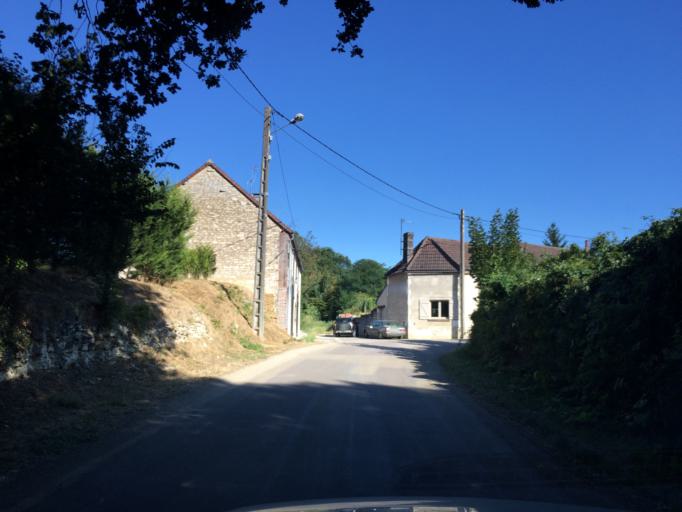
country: FR
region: Bourgogne
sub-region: Departement de l'Yonne
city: Fleury-la-Vallee
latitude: 47.9025
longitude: 3.4468
